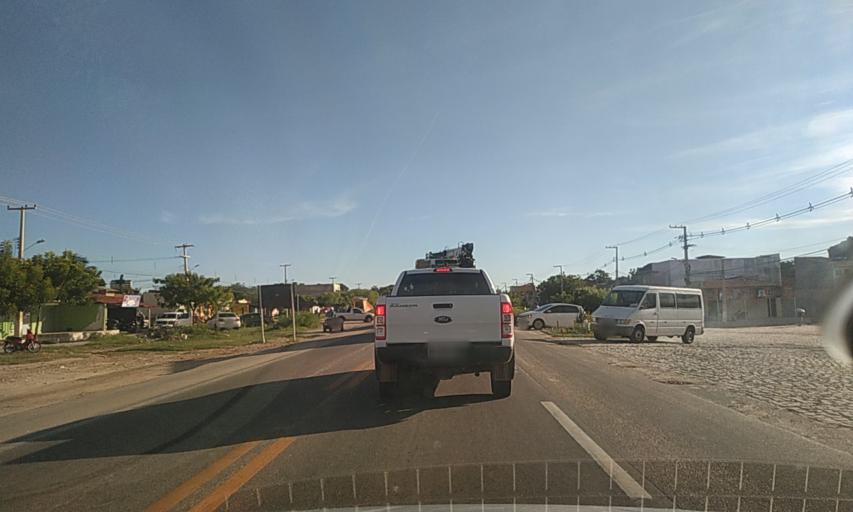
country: BR
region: Rio Grande do Norte
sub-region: Mossoro
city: Mossoro
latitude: -5.1964
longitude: -37.3163
